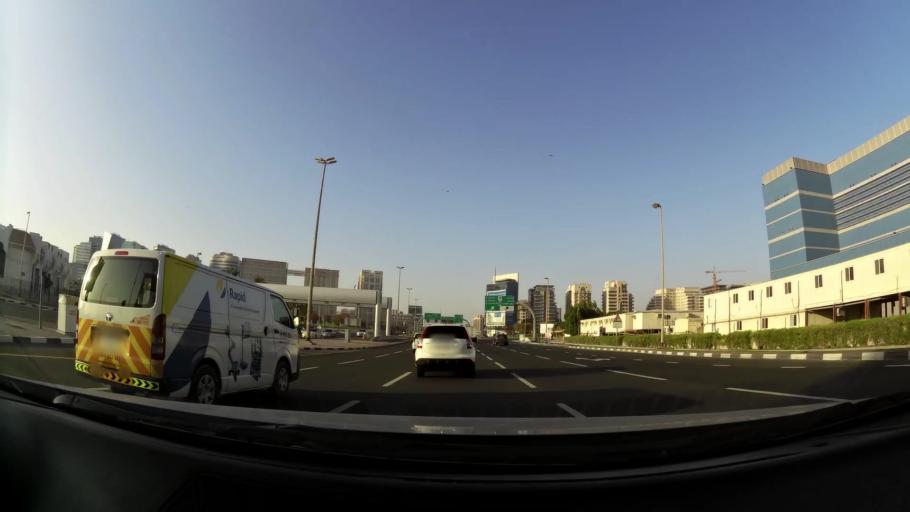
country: AE
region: Ash Shariqah
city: Sharjah
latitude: 25.2532
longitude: 55.3224
